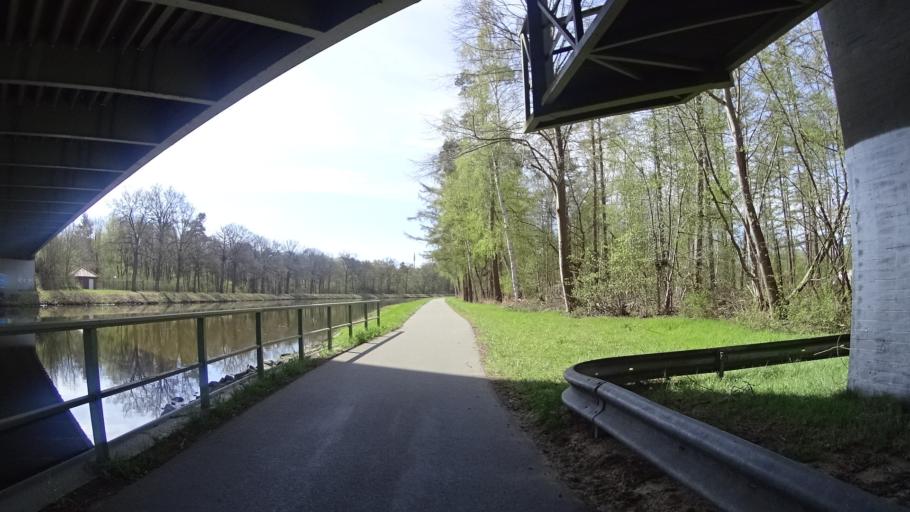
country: DE
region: Lower Saxony
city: Lingen
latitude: 52.5714
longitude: 7.3097
